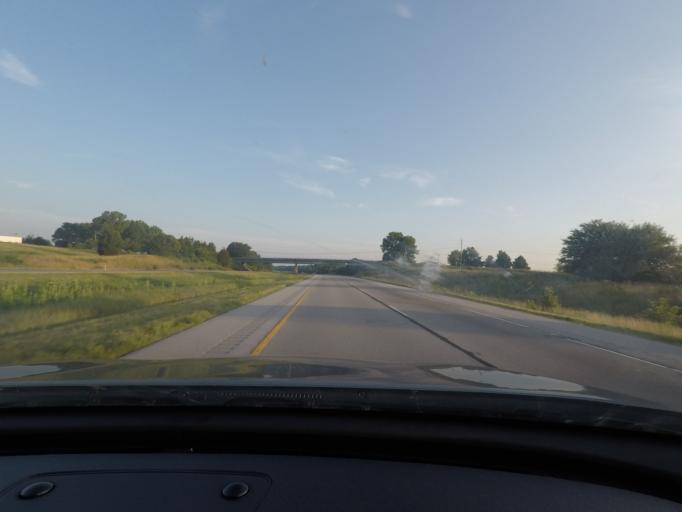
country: US
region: Illinois
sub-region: Johnson County
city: Goreville
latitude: 37.5786
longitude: -88.9627
